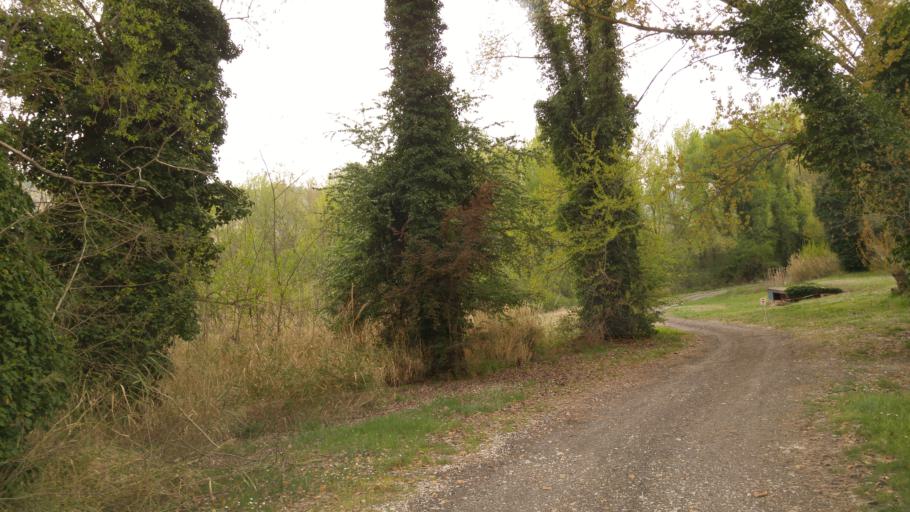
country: IT
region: The Marches
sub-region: Provincia di Pesaro e Urbino
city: Bellocchi
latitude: 43.7705
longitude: 12.9887
